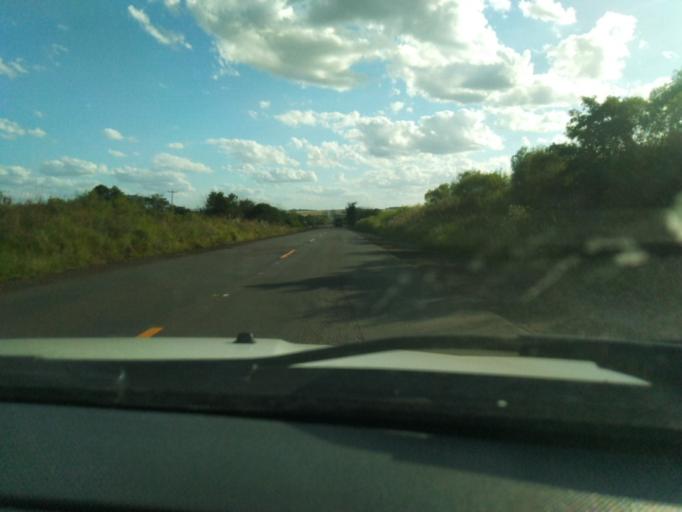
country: AR
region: Corrientes
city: Garruchos
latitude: -28.5537
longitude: -55.5719
